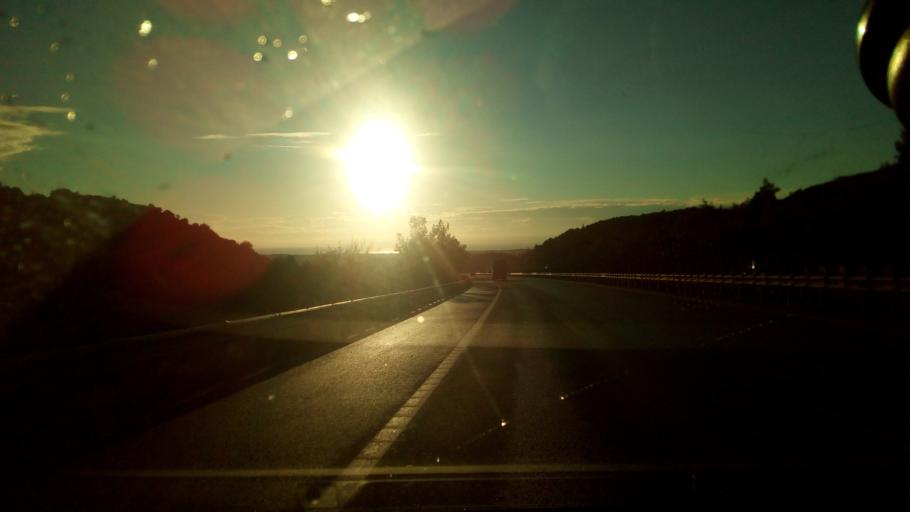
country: CY
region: Larnaka
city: Kofinou
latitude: 34.8516
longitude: 33.3982
